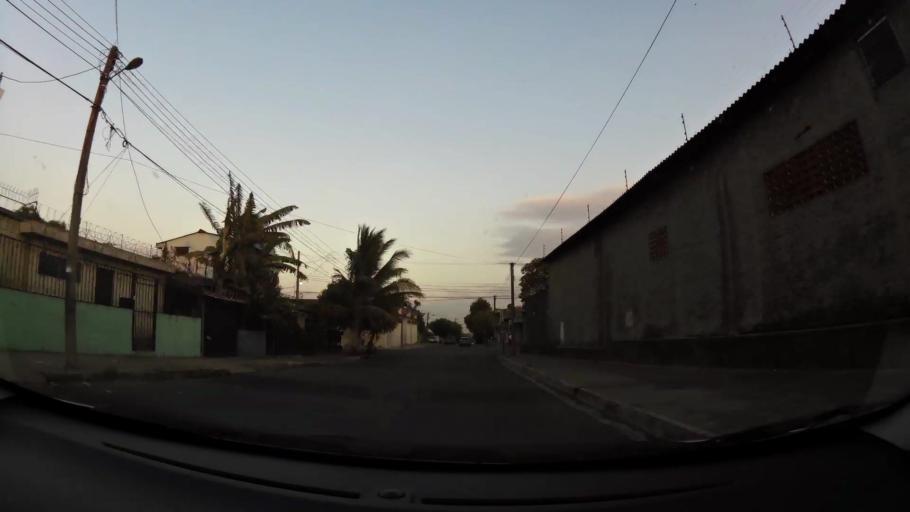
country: SV
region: San Salvador
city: Delgado
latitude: 13.7113
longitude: -89.1880
